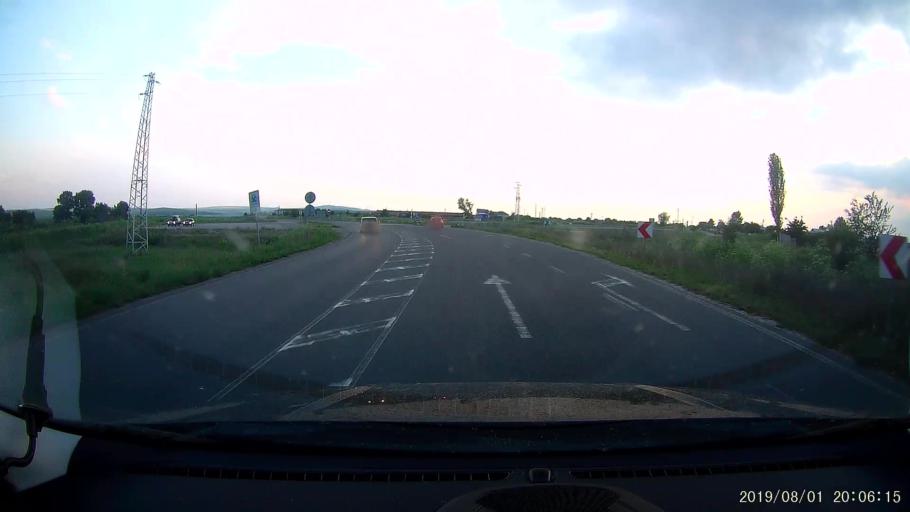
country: BG
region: Yambol
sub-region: Obshtina Yambol
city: Yambol
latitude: 42.5365
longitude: 26.5566
